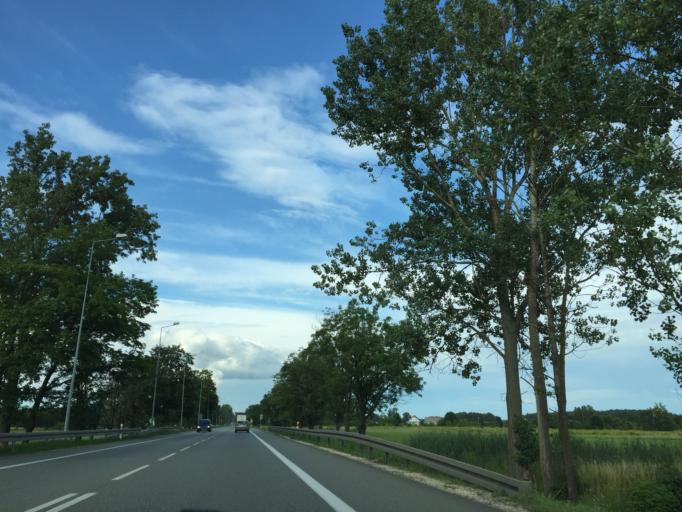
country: PL
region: Masovian Voivodeship
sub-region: Powiat otwocki
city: Karczew
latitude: 52.0192
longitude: 21.2948
